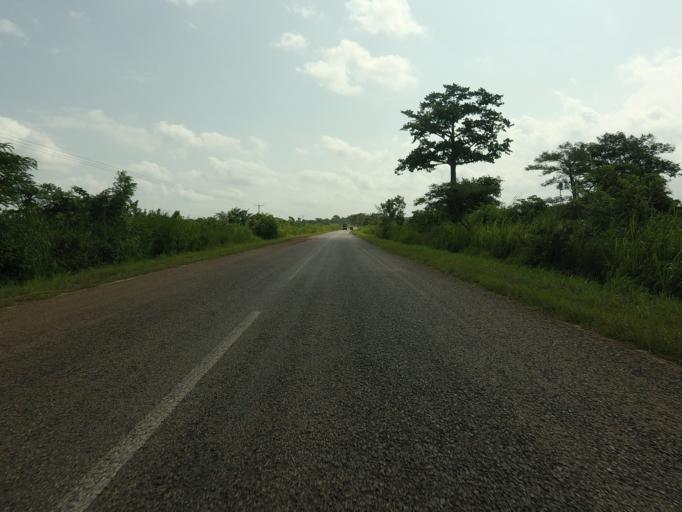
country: GH
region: Volta
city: Ho
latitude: 6.3937
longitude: 0.8047
